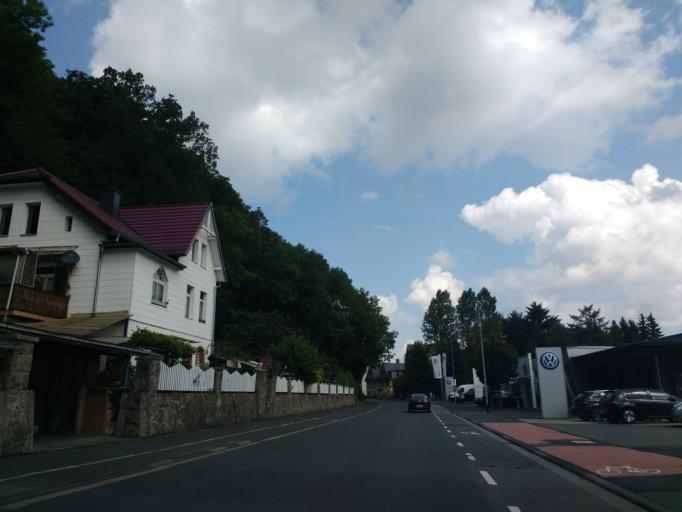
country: DE
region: Hesse
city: Herborn
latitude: 50.6882
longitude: 8.3015
